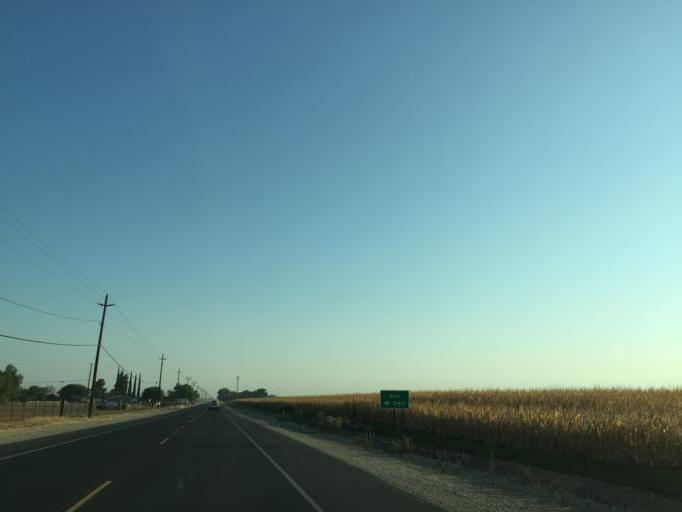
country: US
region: California
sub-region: Tulare County
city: Visalia
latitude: 36.4054
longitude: -119.2962
